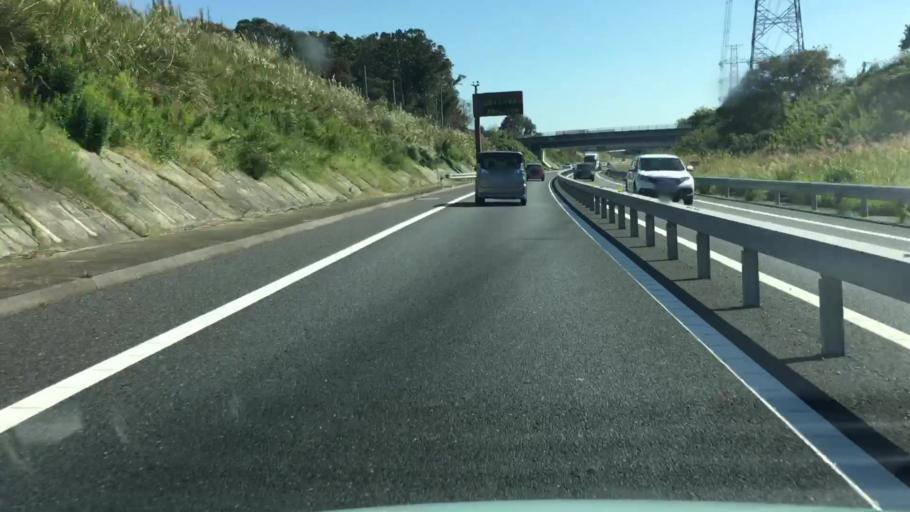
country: JP
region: Ibaraki
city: Ushiku
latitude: 35.9931
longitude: 140.1729
